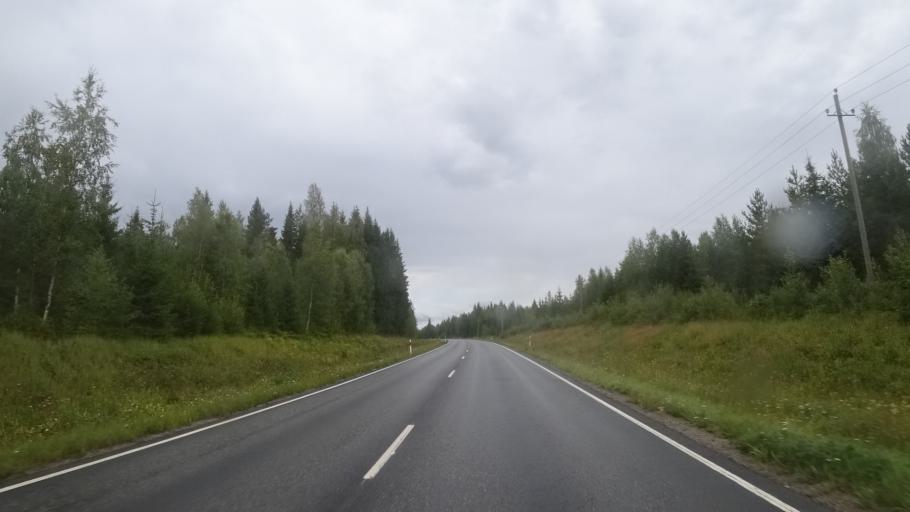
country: FI
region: Southern Savonia
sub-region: Savonlinna
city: Kerimaeki
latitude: 62.0095
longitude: 29.3354
